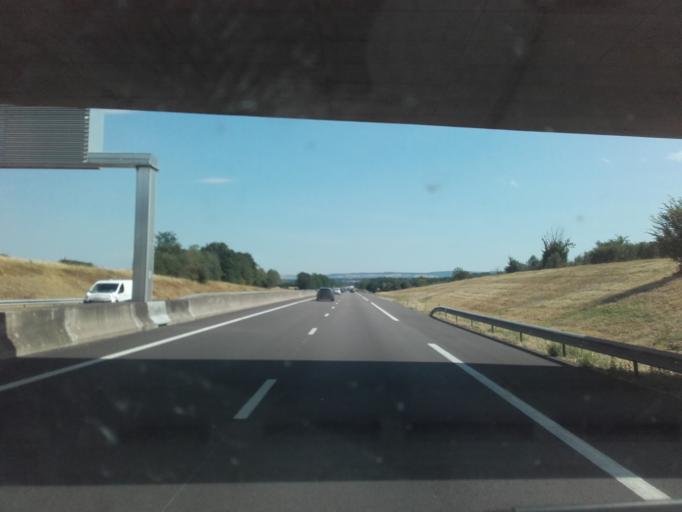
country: FR
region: Bourgogne
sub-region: Departement de la Cote-d'Or
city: Semur-en-Auxois
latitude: 47.4134
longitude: 4.3372
